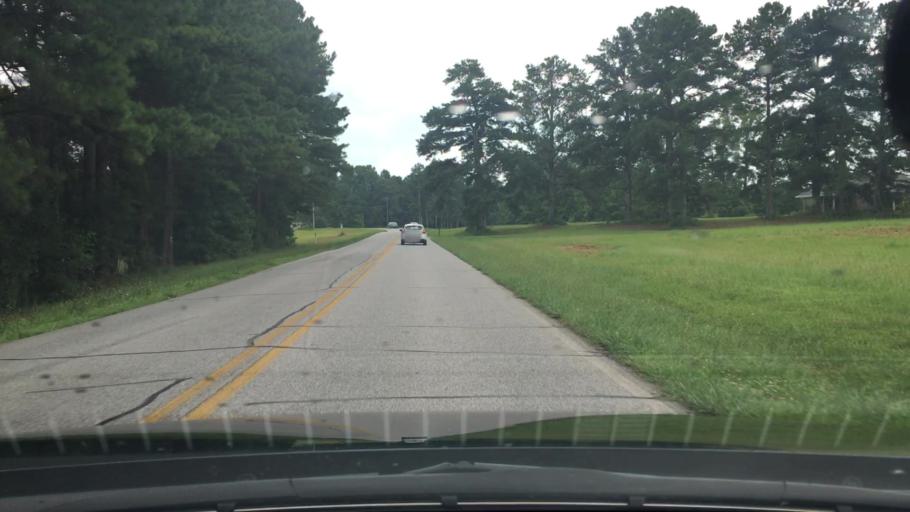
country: US
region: Georgia
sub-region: Coweta County
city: East Newnan
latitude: 33.3998
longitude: -84.6972
